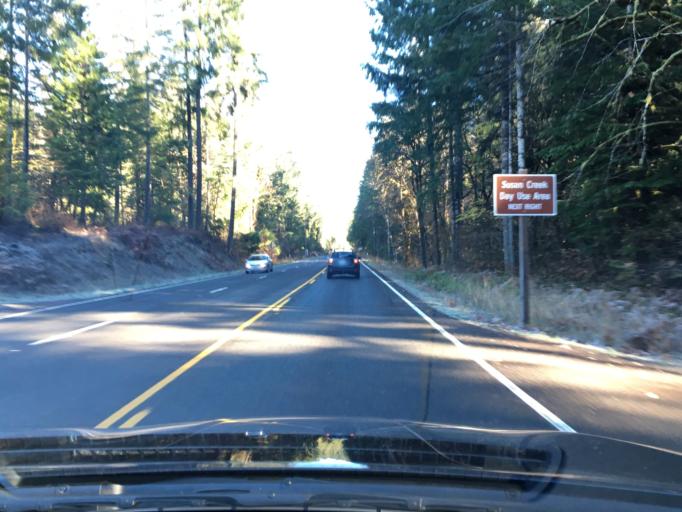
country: US
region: Oregon
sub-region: Douglas County
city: Glide
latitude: 43.2977
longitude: -122.9099
